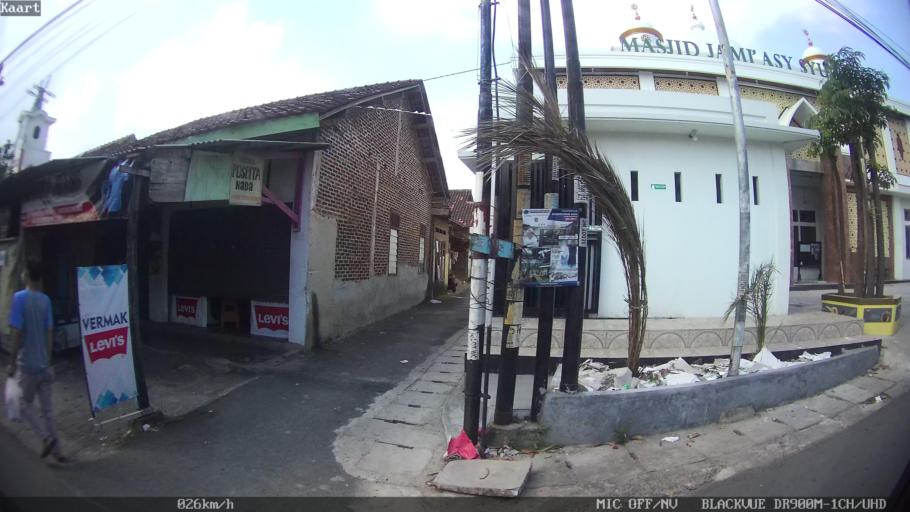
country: ID
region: Lampung
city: Kedaton
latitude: -5.3929
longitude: 105.2165
